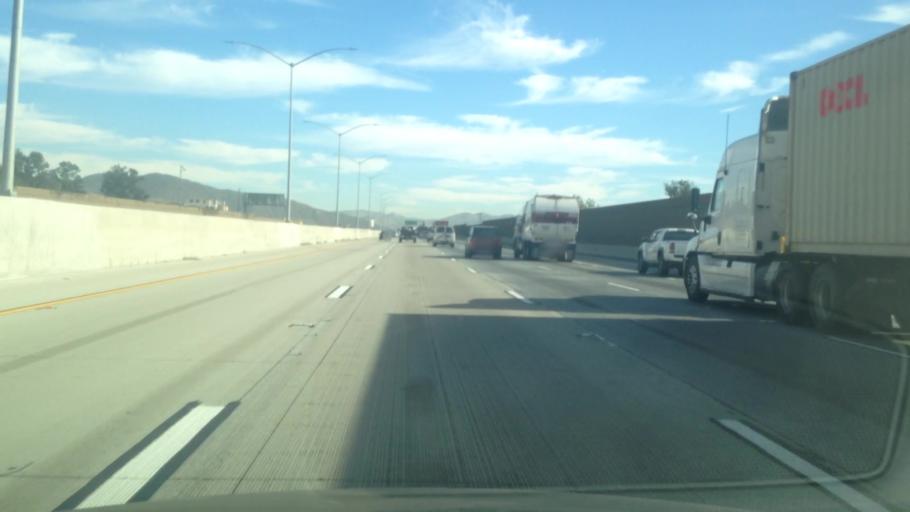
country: US
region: California
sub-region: Riverside County
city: Sunnyslope
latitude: 34.0146
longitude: -117.4525
